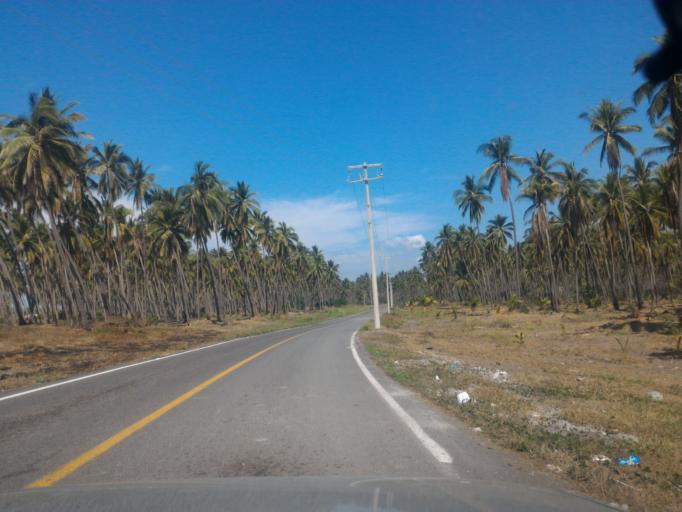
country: MX
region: Colima
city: Armeria
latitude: 18.8439
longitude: -103.9484
